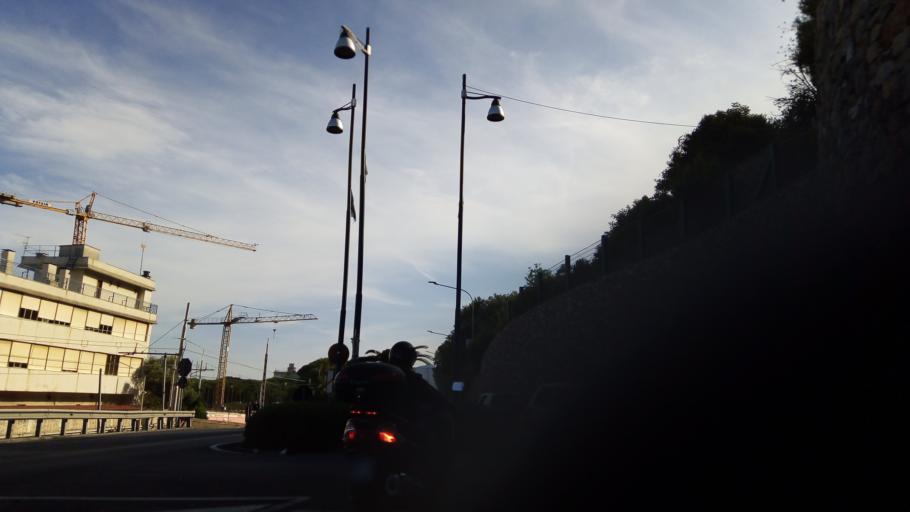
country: IT
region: Liguria
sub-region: Provincia di Savona
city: Borghetto Santo Spirito
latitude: 44.1015
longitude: 8.2363
